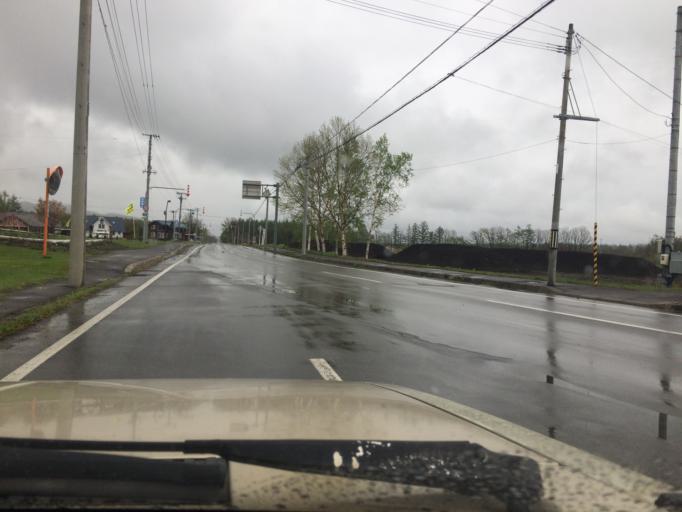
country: JP
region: Hokkaido
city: Obihiro
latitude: 42.8062
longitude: 142.9587
